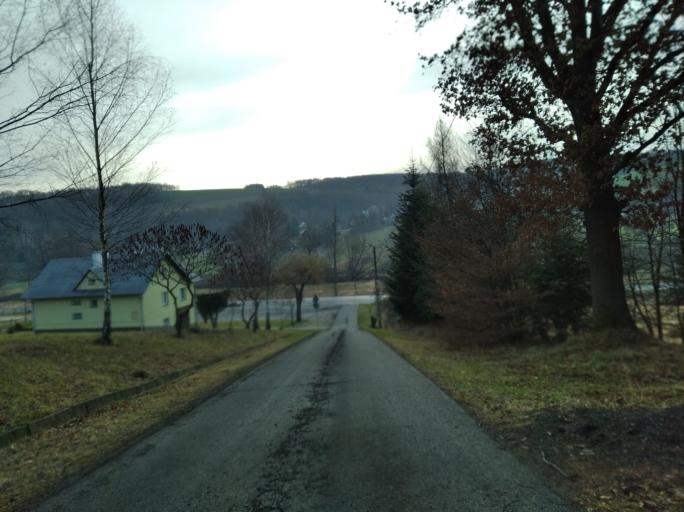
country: PL
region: Subcarpathian Voivodeship
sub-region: Powiat strzyzowski
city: Czudec
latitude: 49.9256
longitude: 21.8000
